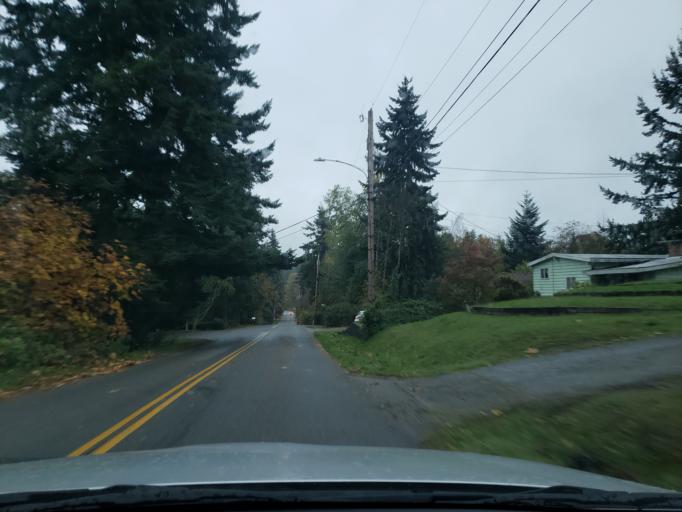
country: US
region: Washington
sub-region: Snohomish County
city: Meadowdale
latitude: 47.8348
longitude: -122.3306
